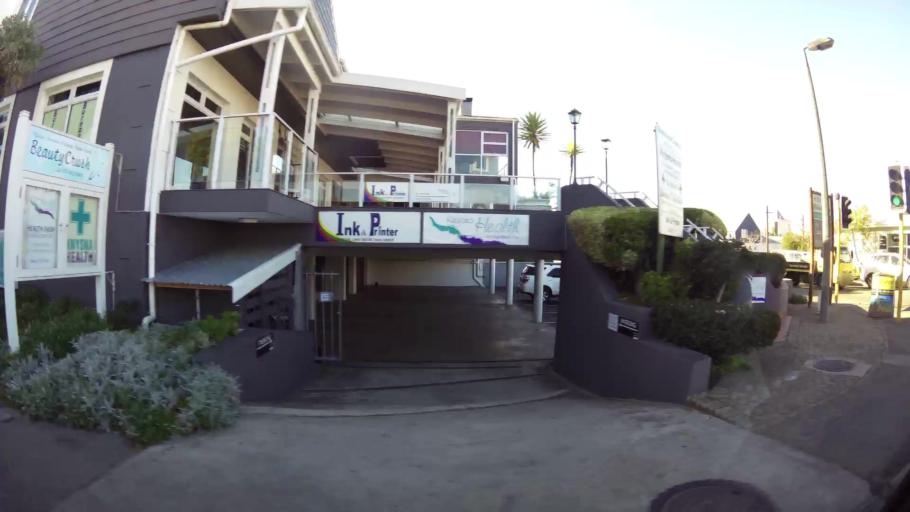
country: ZA
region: Western Cape
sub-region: Eden District Municipality
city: Knysna
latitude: -34.0398
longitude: 23.0453
